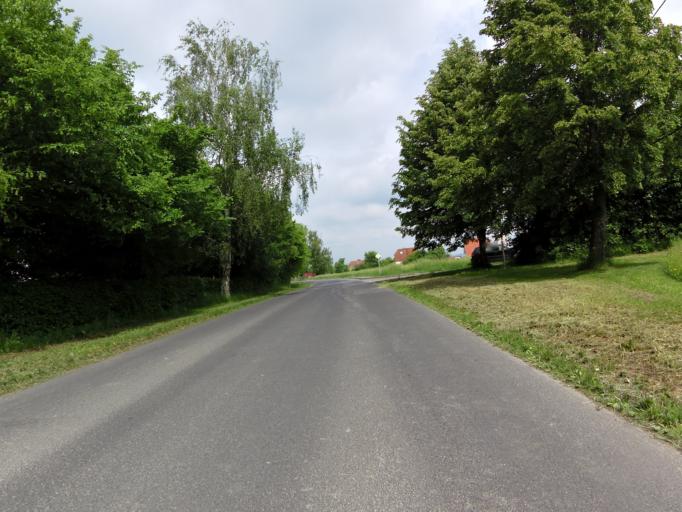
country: DE
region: Bavaria
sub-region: Regierungsbezirk Unterfranken
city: Eisingen
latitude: 49.7544
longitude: 9.8320
